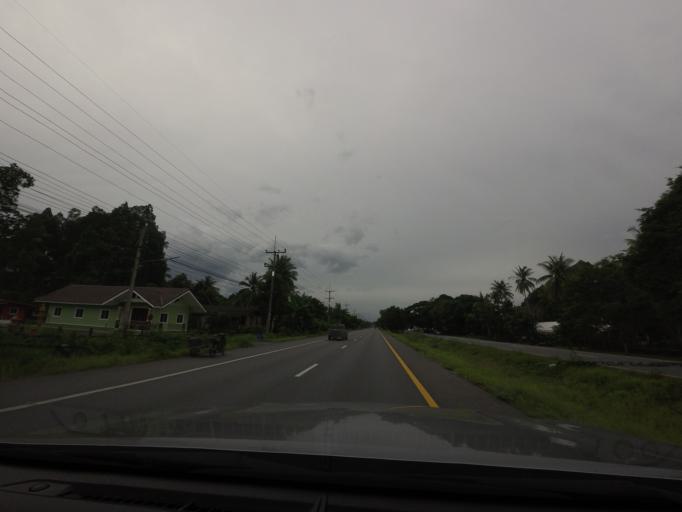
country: TH
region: Nakhon Si Thammarat
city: Chaloem Phra Kiat
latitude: 8.1641
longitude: 100.0511
